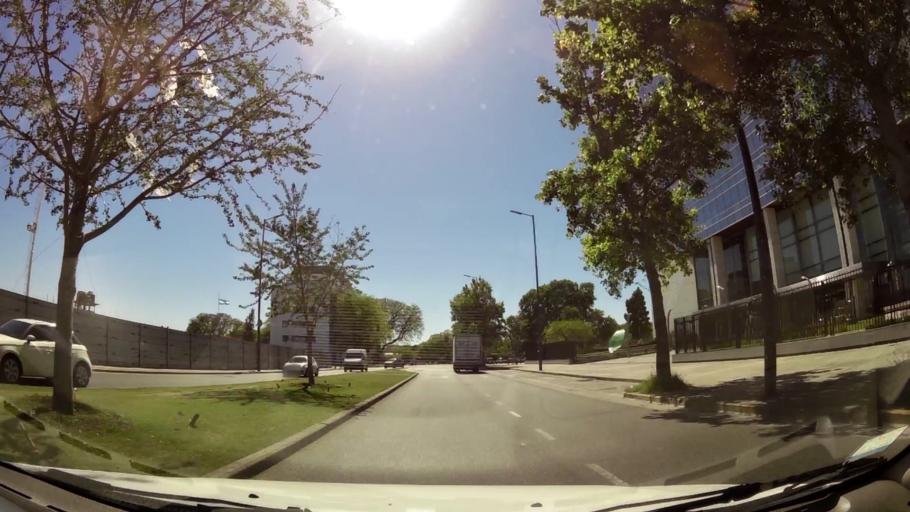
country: AR
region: Buenos Aires F.D.
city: Buenos Aires
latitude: -34.5985
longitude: -58.3653
